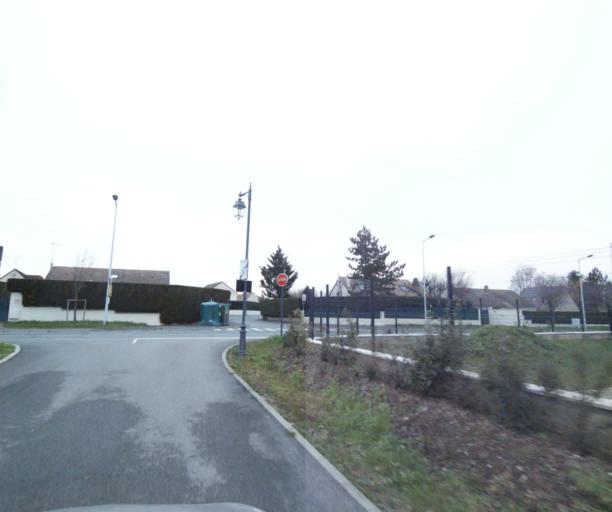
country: FR
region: Ile-de-France
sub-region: Departement de Seine-et-Marne
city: Dammartin-en-Goele
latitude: 49.0635
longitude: 2.6884
